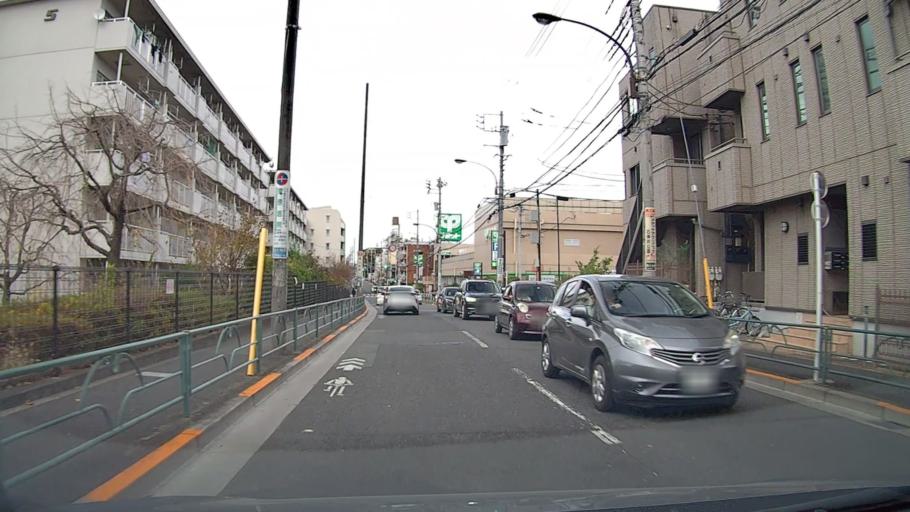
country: JP
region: Saitama
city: Wako
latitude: 35.7453
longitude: 139.6082
